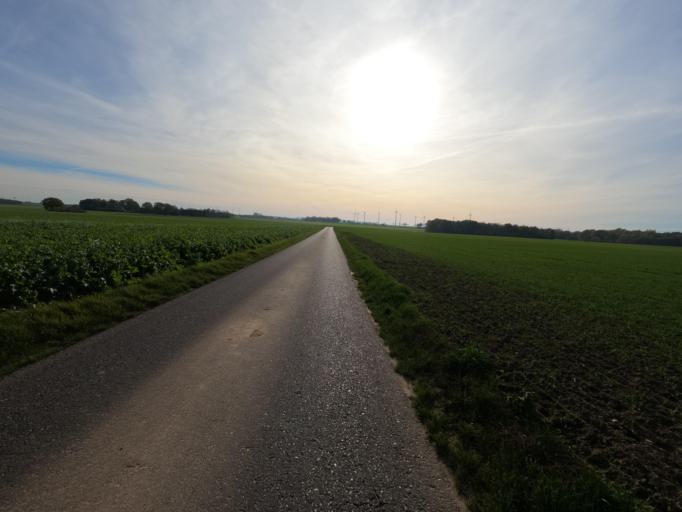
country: DE
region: North Rhine-Westphalia
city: Erkelenz
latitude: 51.0652
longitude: 6.3749
